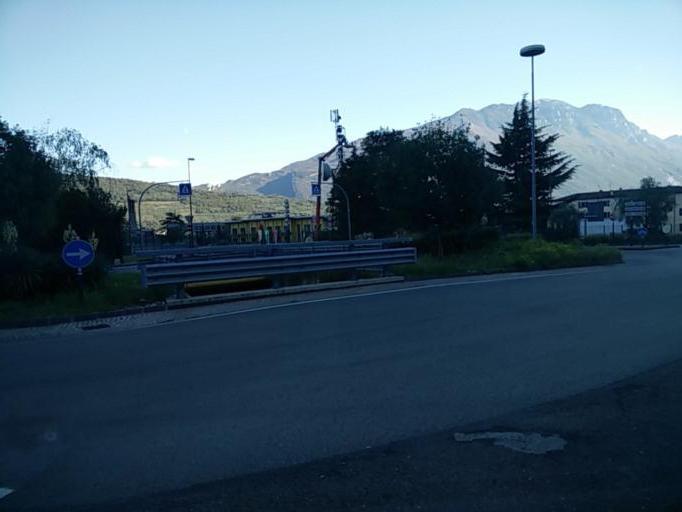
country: IT
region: Trentino-Alto Adige
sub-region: Provincia di Trento
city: Riva del Garda
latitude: 45.8946
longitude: 10.8432
